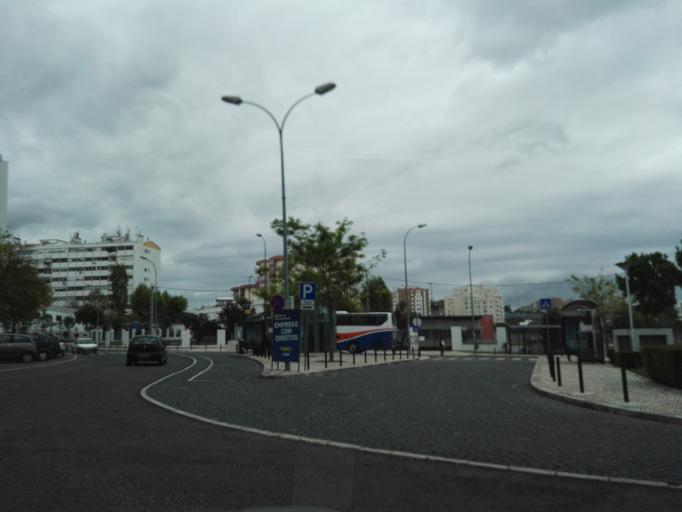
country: PT
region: Lisbon
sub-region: Odivelas
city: Olival do Basto
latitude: 38.7793
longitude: -9.1600
